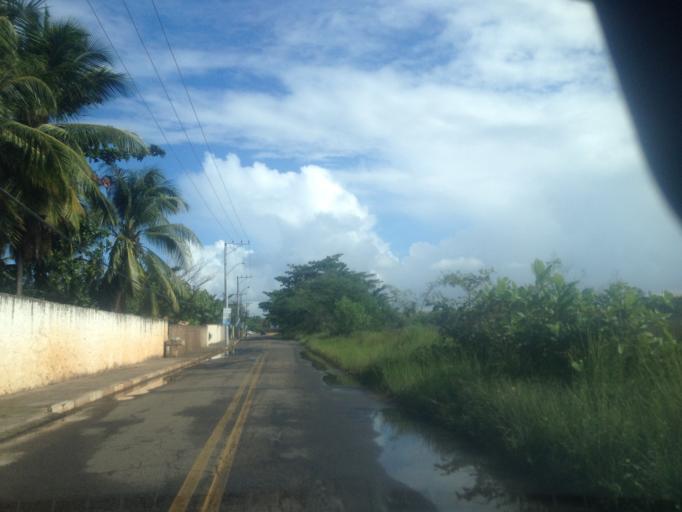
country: BR
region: Bahia
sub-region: Mata De Sao Joao
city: Mata de Sao Joao
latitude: -12.6101
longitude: -38.0426
